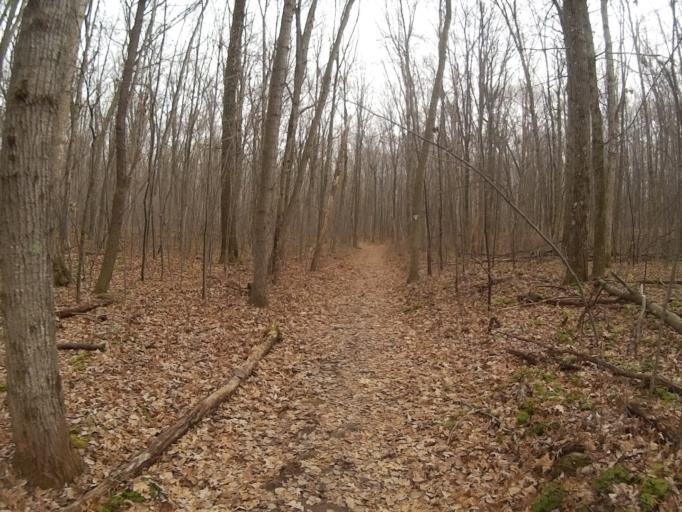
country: US
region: Pennsylvania
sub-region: Centre County
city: Park Forest Village
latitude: 40.7867
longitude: -77.9222
